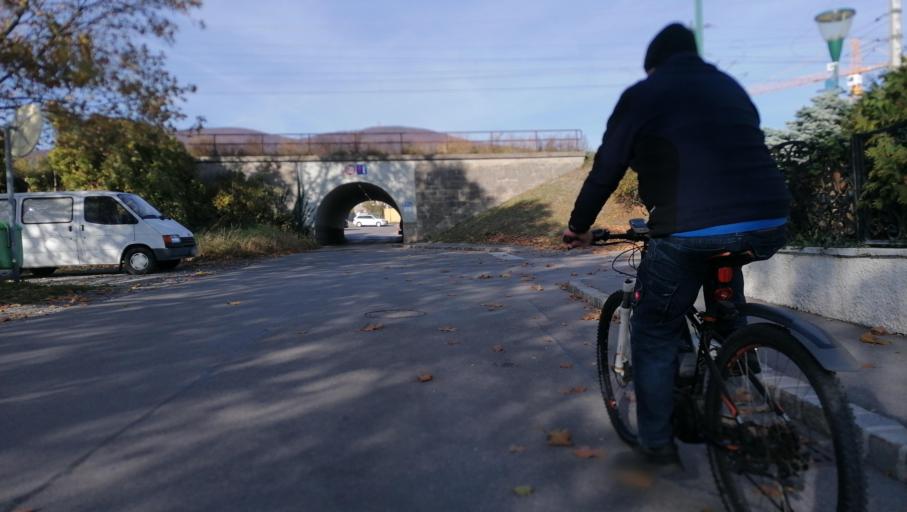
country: AT
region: Lower Austria
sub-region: Politischer Bezirk Modling
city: Gumpoldskirchen
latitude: 48.0388
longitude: 16.2832
